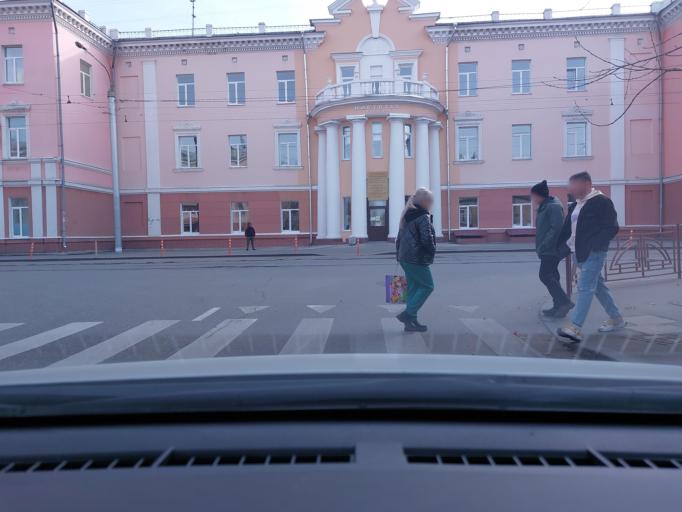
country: RU
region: Irkutsk
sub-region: Irkutskiy Rayon
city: Irkutsk
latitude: 52.2796
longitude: 104.2930
